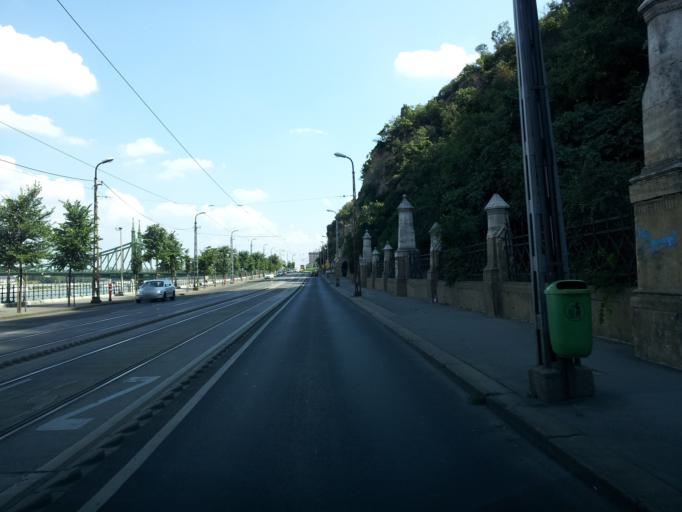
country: HU
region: Budapest
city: Budapest I. keruelet
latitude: 47.4873
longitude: 19.0502
